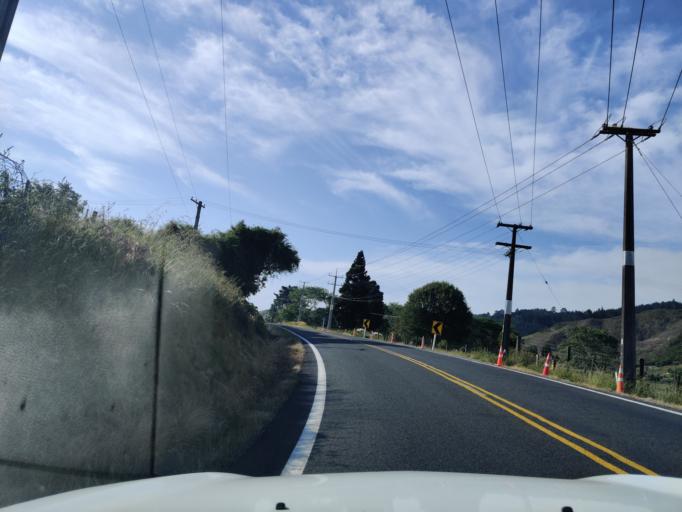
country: NZ
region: Waikato
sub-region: Waikato District
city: Ngaruawahia
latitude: -37.6134
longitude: 175.1807
